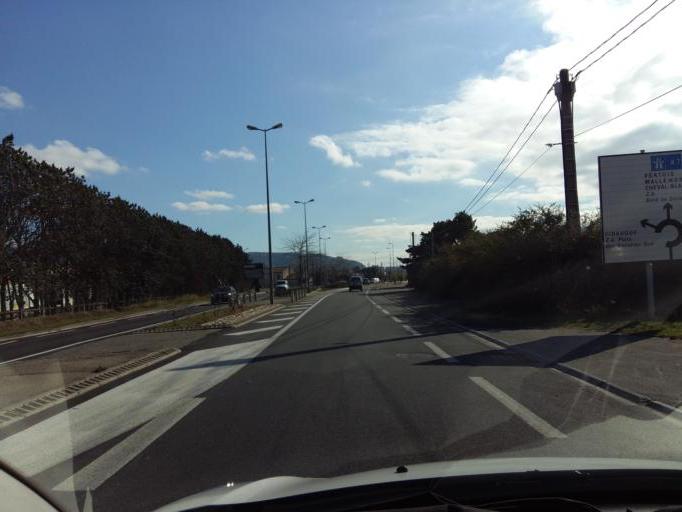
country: FR
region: Provence-Alpes-Cote d'Azur
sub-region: Departement du Vaucluse
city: Cavaillon
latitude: 43.8296
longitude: 5.0560
